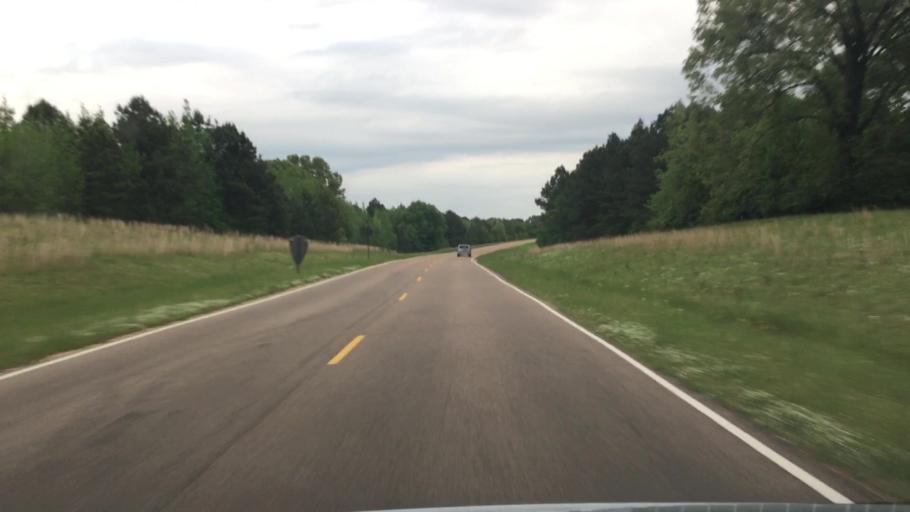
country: US
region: Mississippi
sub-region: Hinds County
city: Clinton
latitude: 32.3928
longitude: -90.2501
